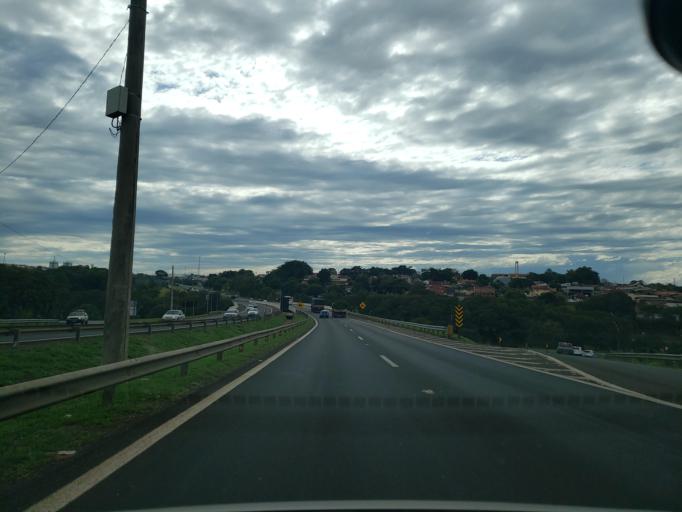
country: BR
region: Sao Paulo
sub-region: Bauru
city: Bauru
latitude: -22.3123
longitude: -49.0558
